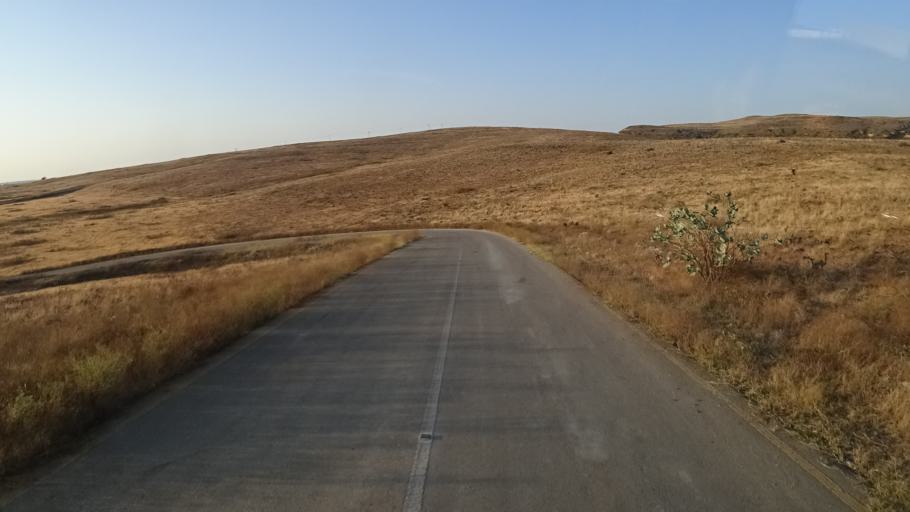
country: OM
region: Zufar
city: Salalah
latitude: 17.1541
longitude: 54.6220
